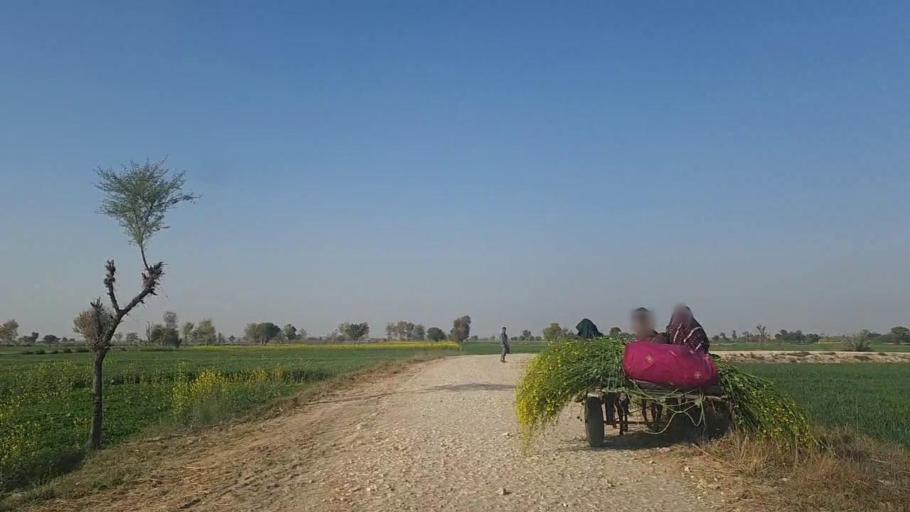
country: PK
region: Sindh
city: Jam Sahib
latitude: 26.3334
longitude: 68.7143
